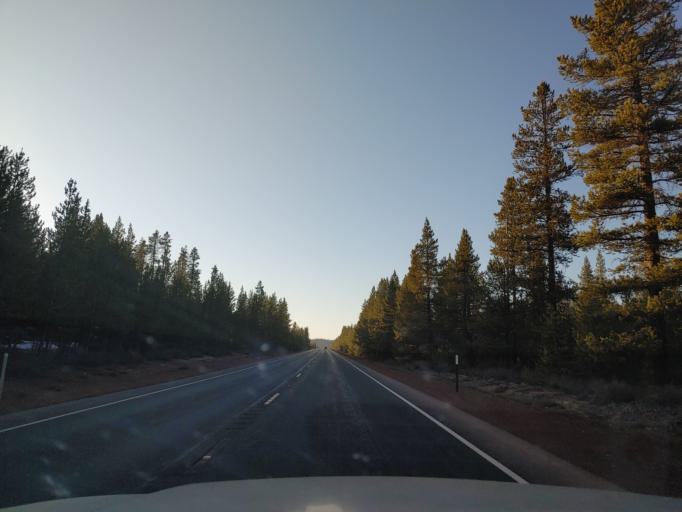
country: US
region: Oregon
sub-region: Deschutes County
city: La Pine
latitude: 43.4215
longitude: -121.8422
